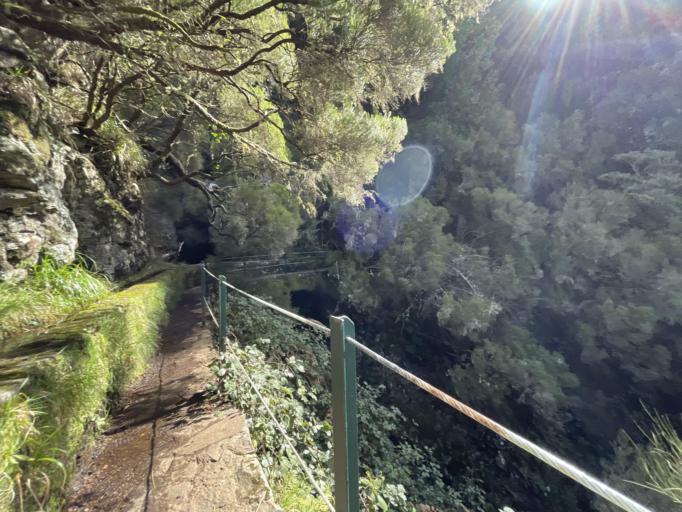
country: PT
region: Madeira
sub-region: Calheta
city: Arco da Calheta
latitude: 32.7657
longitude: -17.1259
